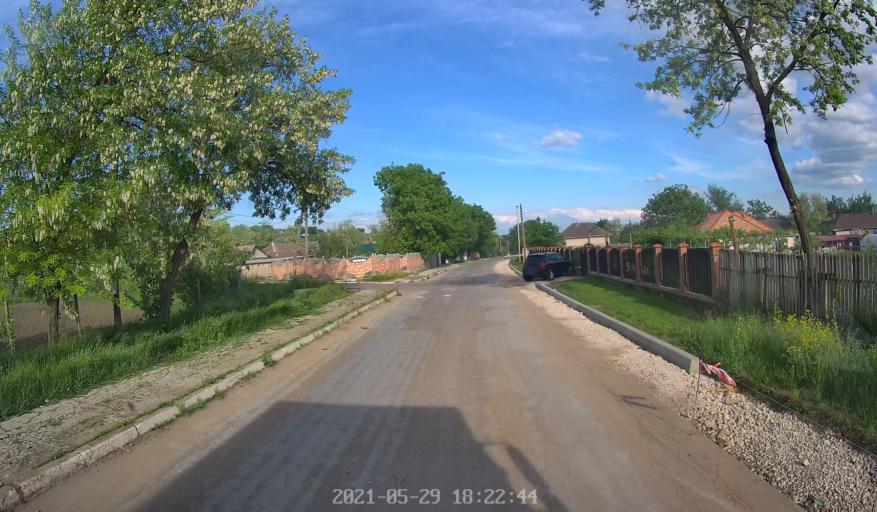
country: MD
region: Laloveni
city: Ialoveni
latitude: 46.8353
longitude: 28.8503
